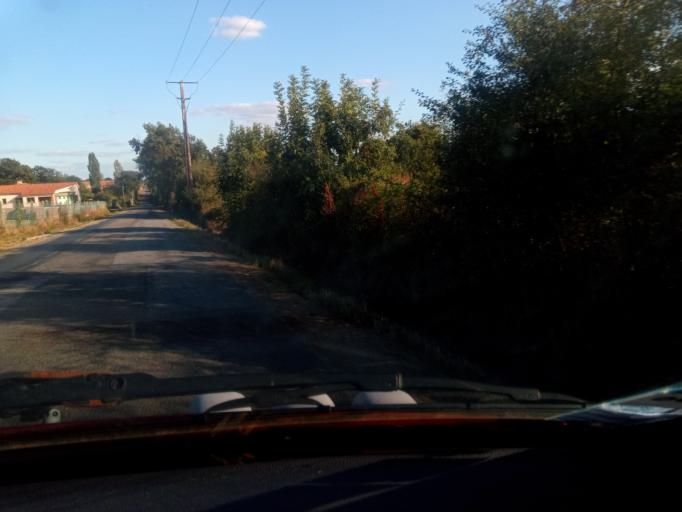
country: FR
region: Poitou-Charentes
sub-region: Departement de la Vienne
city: Availles-Limouzine
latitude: 46.1273
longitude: 0.7219
